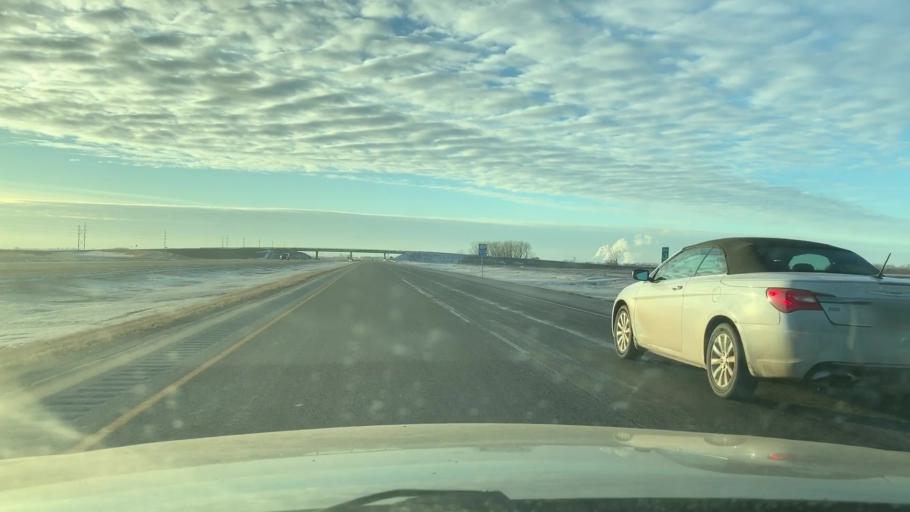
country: US
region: North Dakota
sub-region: Cass County
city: Casselton
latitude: 46.8768
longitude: -97.1524
